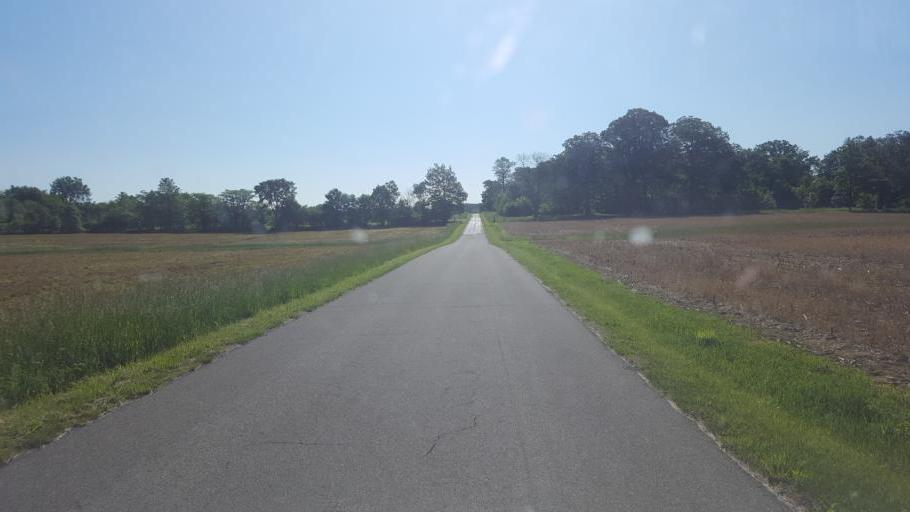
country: US
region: Ohio
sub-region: Crawford County
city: Bucyrus
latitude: 40.7548
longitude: -82.8937
